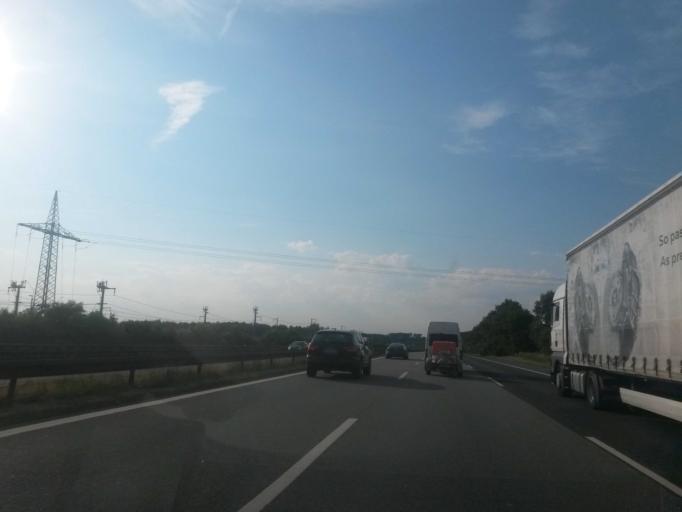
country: DE
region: Bavaria
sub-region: Regierungsbezirk Mittelfranken
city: Hilpoltstein
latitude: 49.1986
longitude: 11.2420
